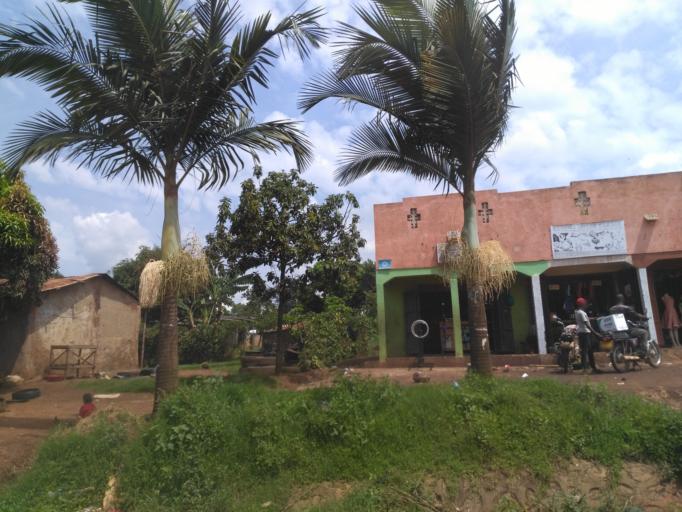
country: UG
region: Central Region
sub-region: Wakiso District
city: Kireka
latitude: 0.4514
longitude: 32.6096
